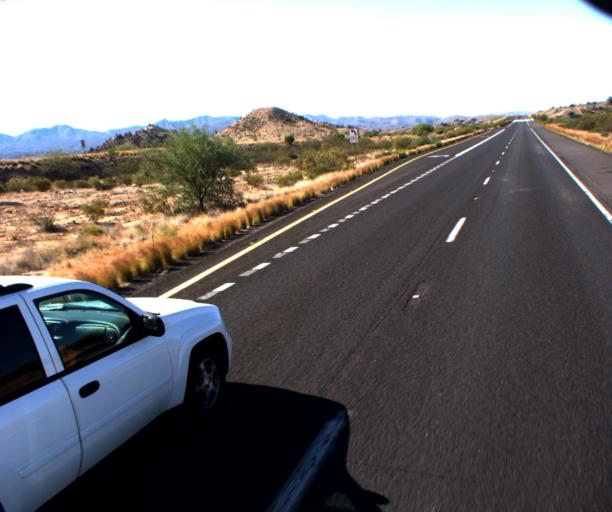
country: US
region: Arizona
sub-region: Mohave County
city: Kingman
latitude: 35.0819
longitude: -113.6661
